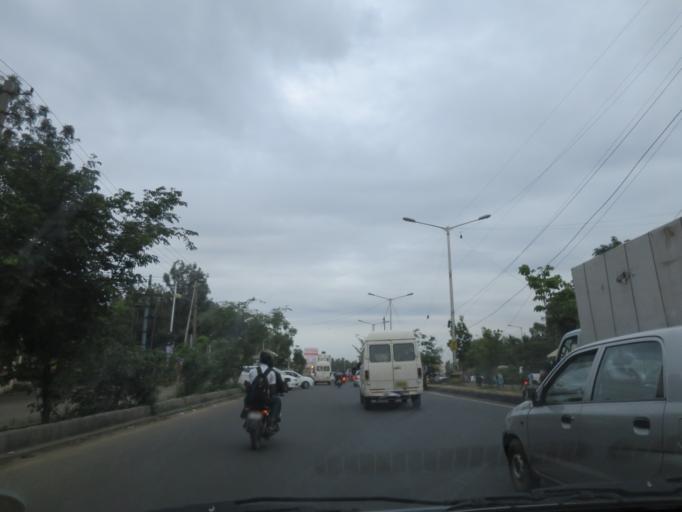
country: IN
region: Karnataka
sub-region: Bangalore Urban
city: Bangalore
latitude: 12.9687
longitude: 77.7013
